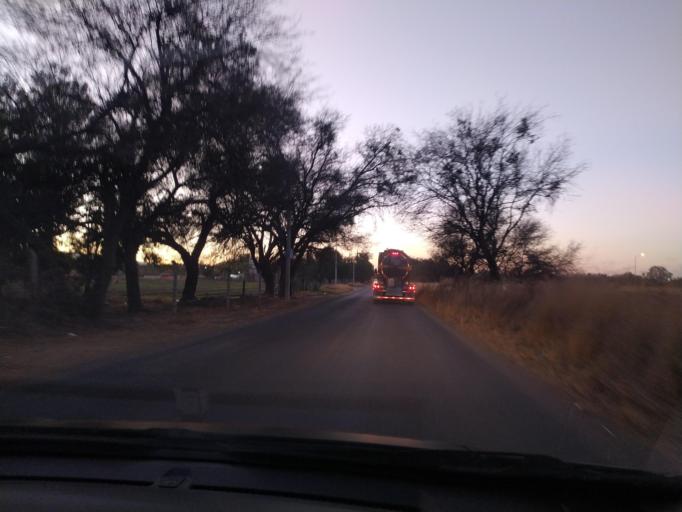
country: MX
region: Guanajuato
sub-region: San Francisco del Rincon
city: Fraccionamiento la Mezquitera
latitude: 21.0190
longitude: -101.8233
